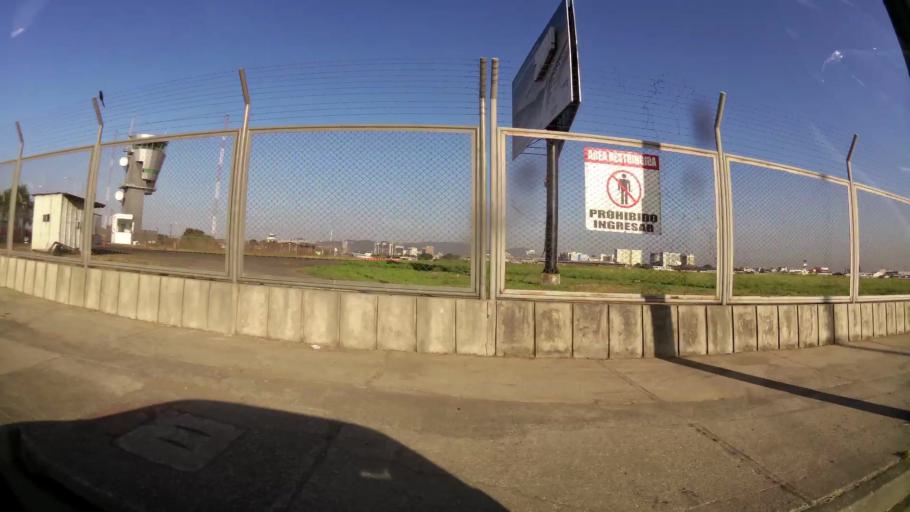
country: EC
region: Guayas
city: Eloy Alfaro
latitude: -2.1583
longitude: -79.8810
